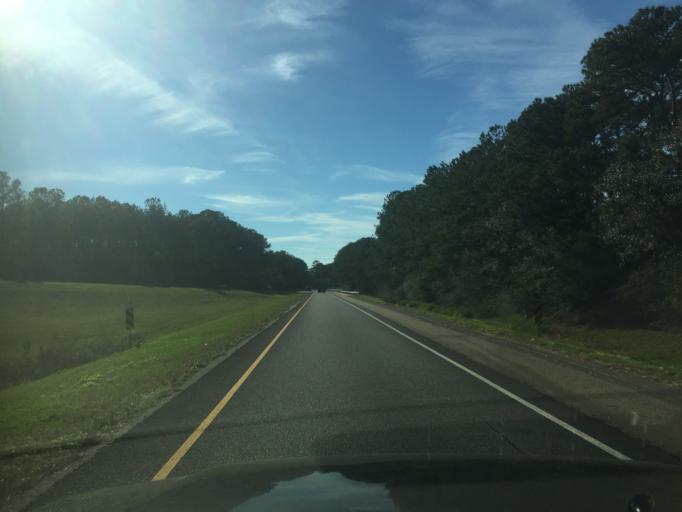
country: US
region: Louisiana
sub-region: Saint Tammany Parish
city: Slidell
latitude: 30.3093
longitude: -89.7416
